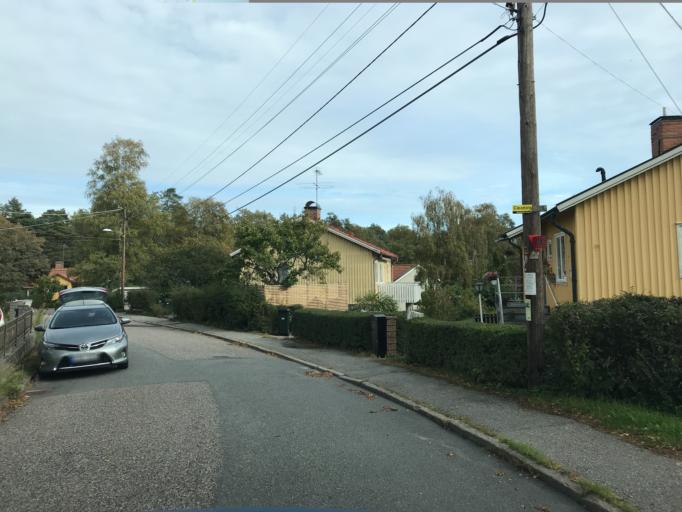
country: SE
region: Stockholm
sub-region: Huddinge Kommun
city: Huddinge
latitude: 59.2730
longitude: 17.9752
